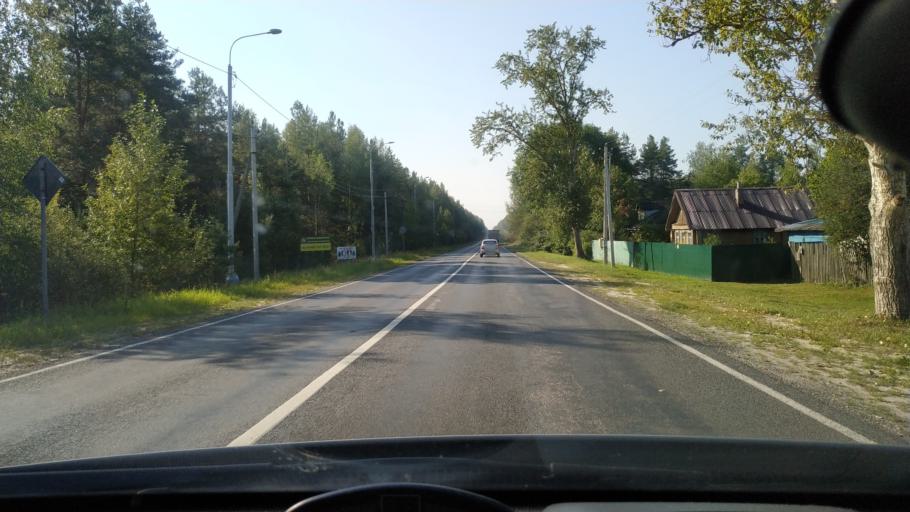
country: RU
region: Moskovskaya
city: Tugolesskiy Bor
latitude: 55.5175
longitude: 39.7115
